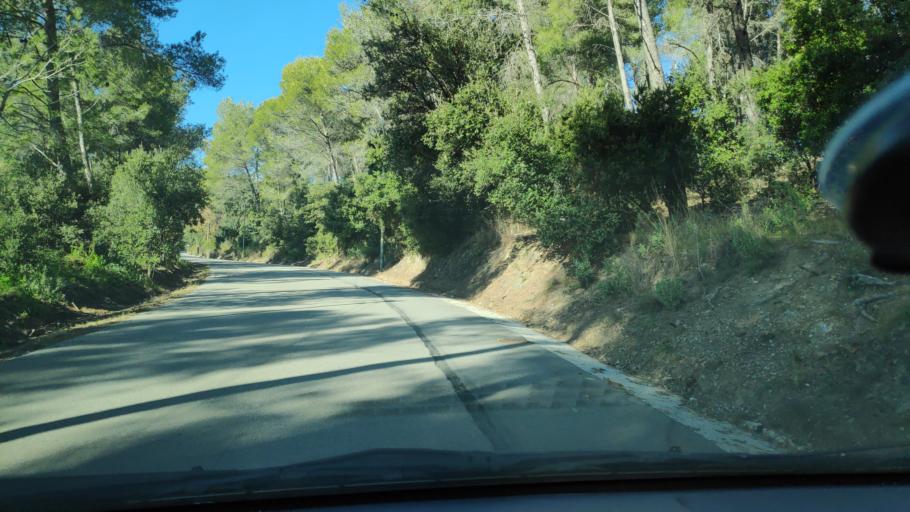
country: ES
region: Catalonia
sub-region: Provincia de Barcelona
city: Matadepera
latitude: 41.5969
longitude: 2.0128
